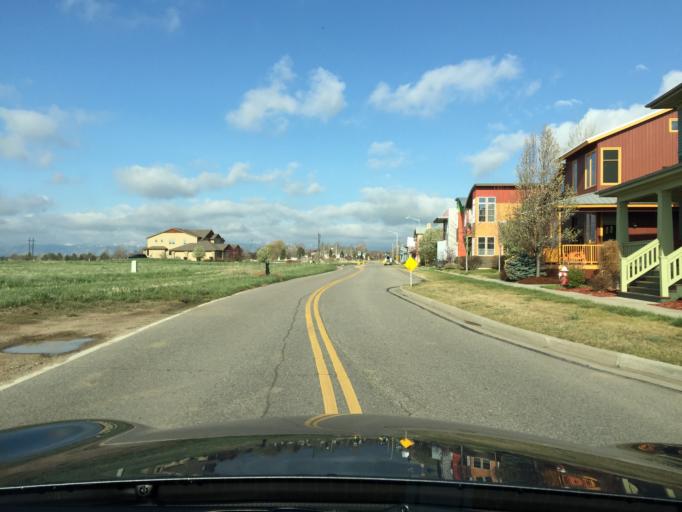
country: US
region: Colorado
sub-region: Boulder County
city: Longmont
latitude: 40.1331
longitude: -105.1056
